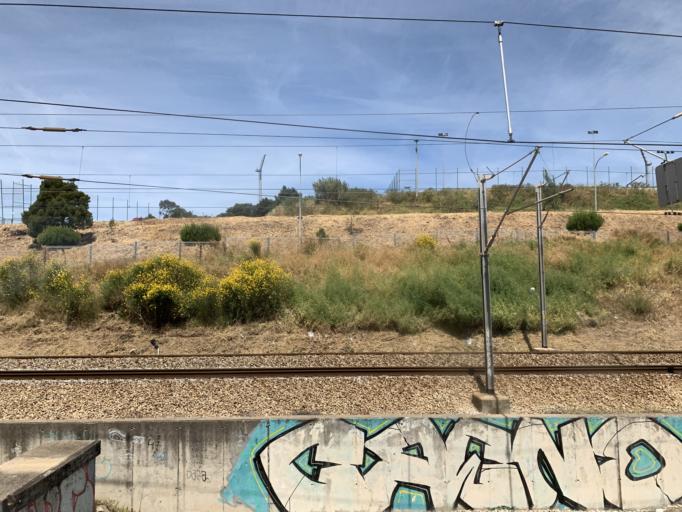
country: PT
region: Lisbon
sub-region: Sintra
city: Queluz
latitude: 38.7503
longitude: -9.2683
